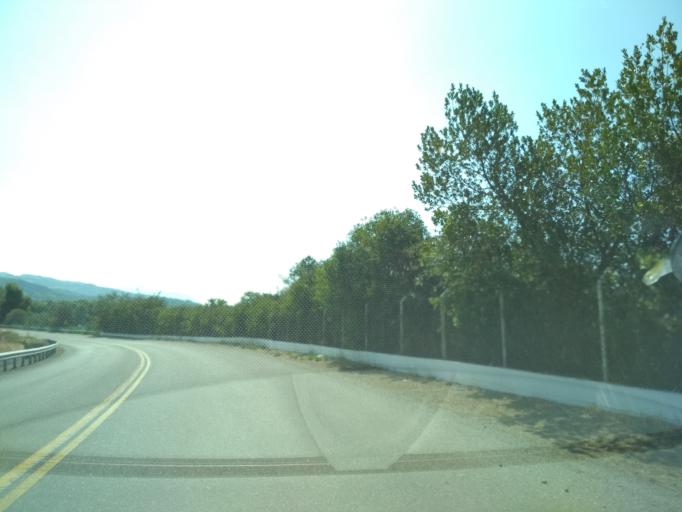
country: GR
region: Central Greece
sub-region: Nomos Evvoias
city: Roviai
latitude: 38.8318
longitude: 23.2005
